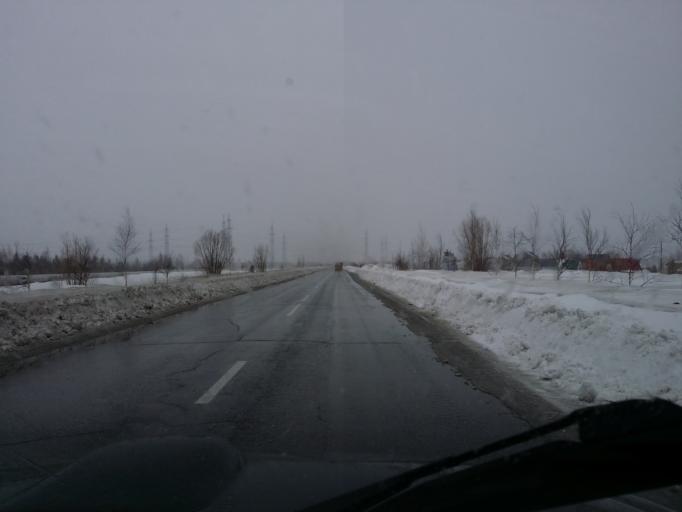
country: RU
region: Khanty-Mansiyskiy Avtonomnyy Okrug
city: Izluchinsk
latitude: 60.9749
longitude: 76.8960
